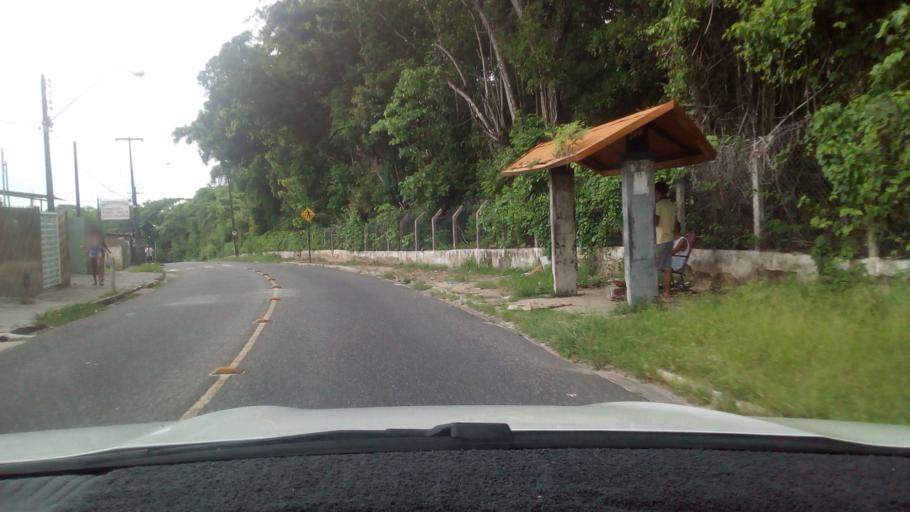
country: BR
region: Paraiba
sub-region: Joao Pessoa
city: Joao Pessoa
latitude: -7.1447
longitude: -34.8695
